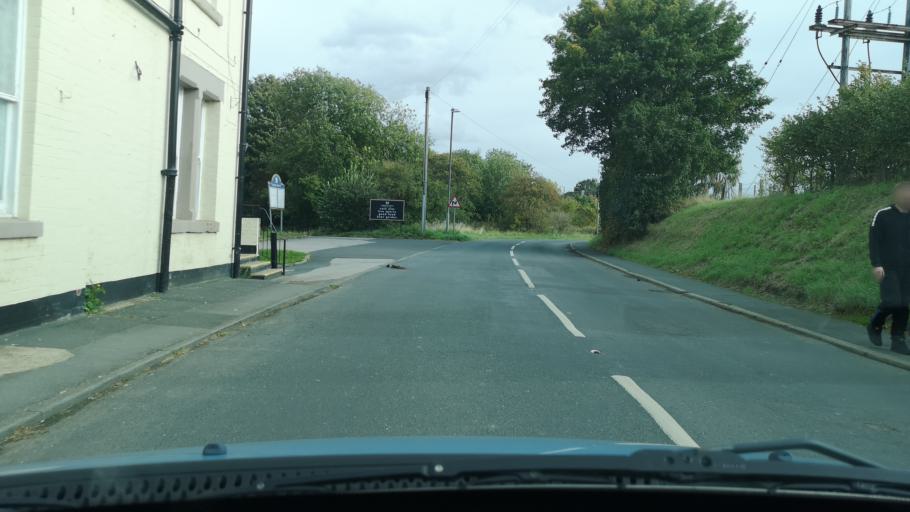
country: GB
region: England
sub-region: City and Borough of Wakefield
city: Sharlston
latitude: 53.6870
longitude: -1.3912
